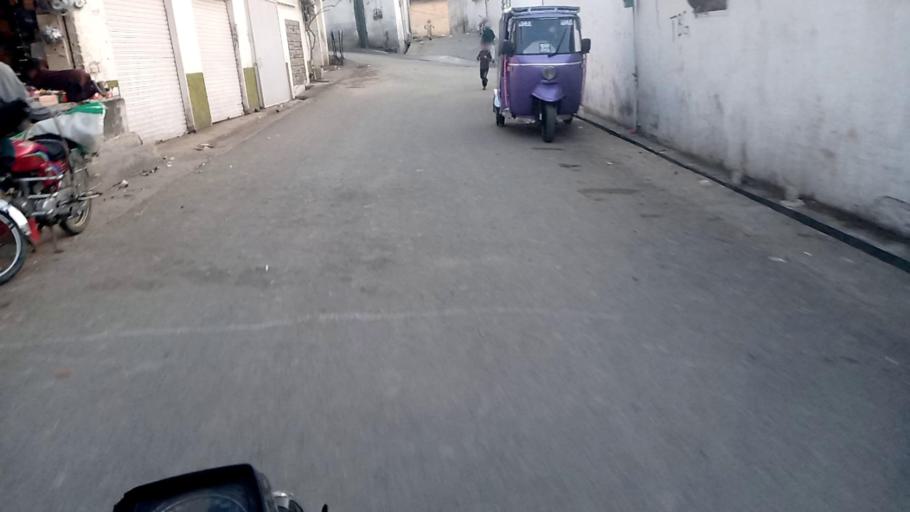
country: PK
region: Khyber Pakhtunkhwa
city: Saidu Sharif
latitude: 34.7552
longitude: 72.3613
